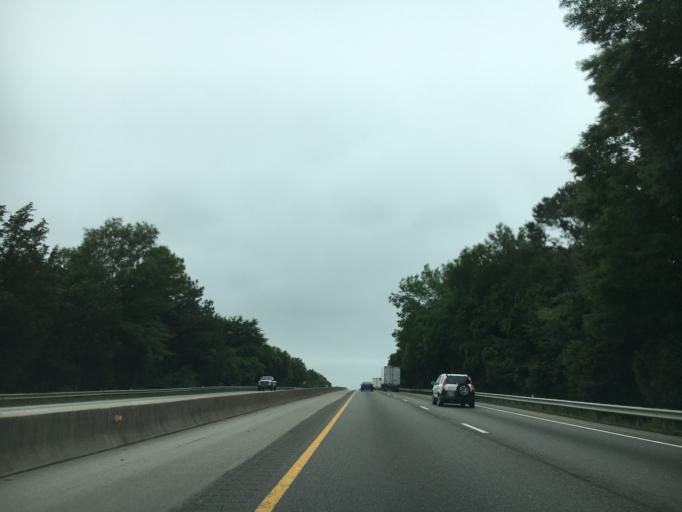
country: US
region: Virginia
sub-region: Chesterfield County
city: Matoaca
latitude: 37.1992
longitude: -77.4524
